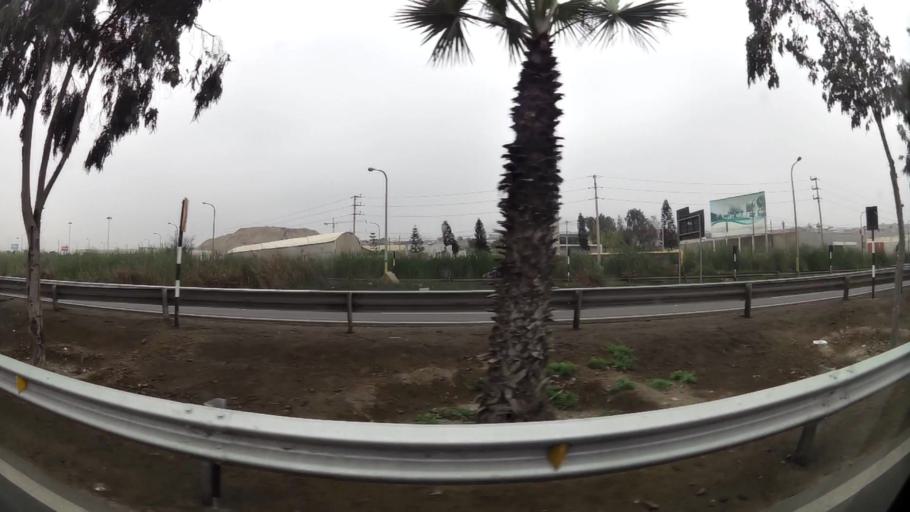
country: PE
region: Lima
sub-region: Lima
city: Surco
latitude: -12.2211
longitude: -76.9760
